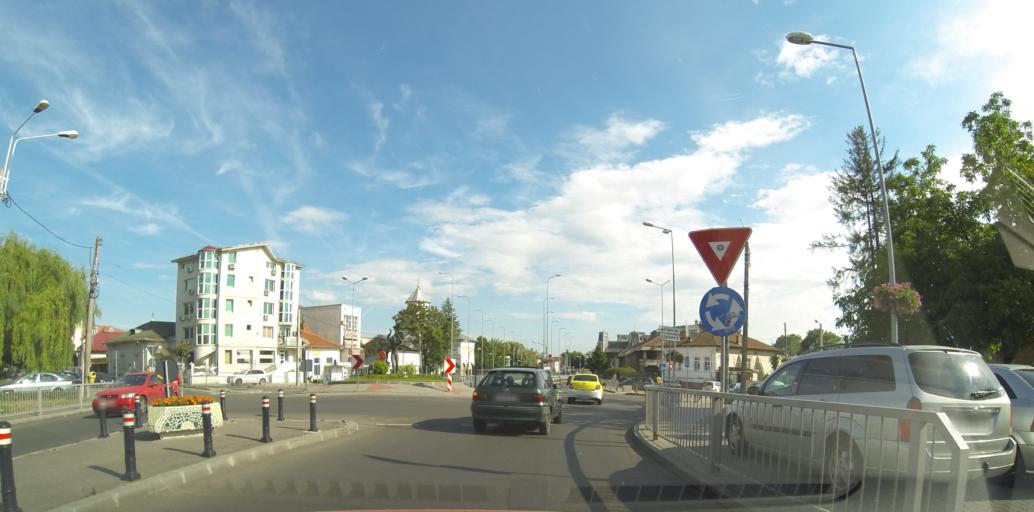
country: RO
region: Dolj
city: Craiova
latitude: 44.3171
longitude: 23.8013
